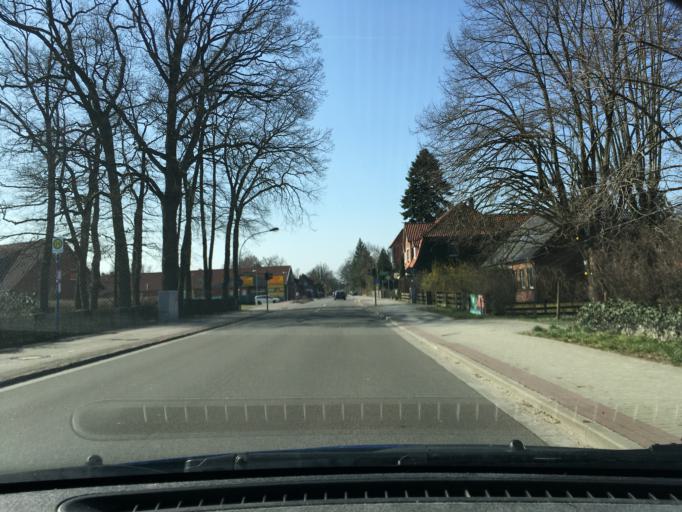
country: DE
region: Lower Saxony
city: Hermannsburg
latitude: 52.8288
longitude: 10.1020
